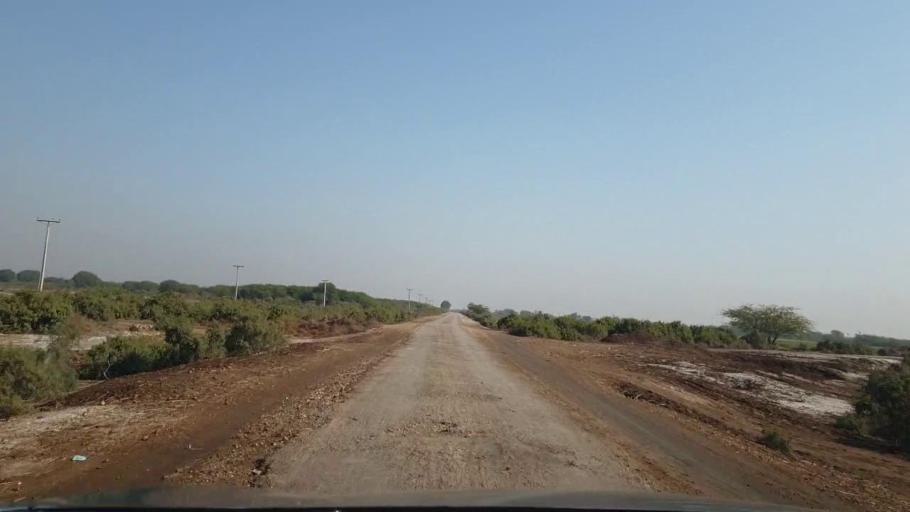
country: PK
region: Sindh
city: Berani
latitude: 25.6276
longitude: 68.8594
